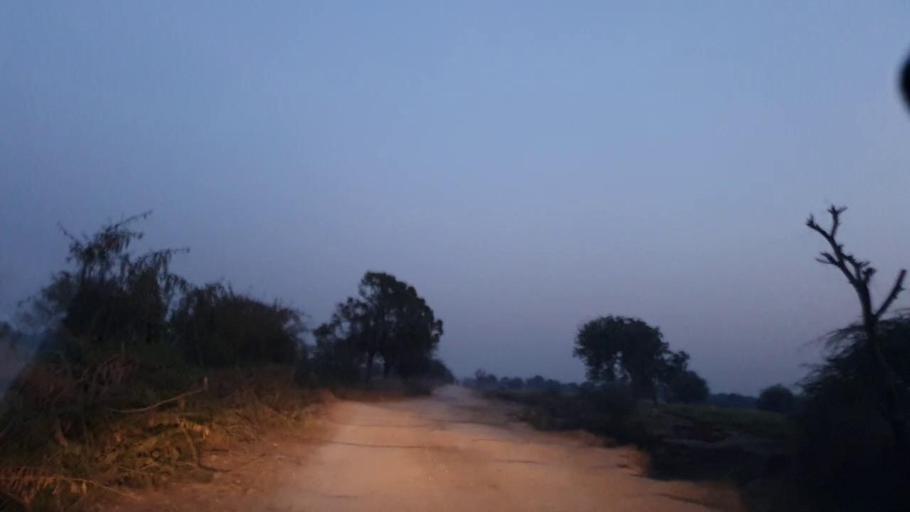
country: PK
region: Sindh
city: Tando Ghulam Ali
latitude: 25.1068
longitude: 68.9084
